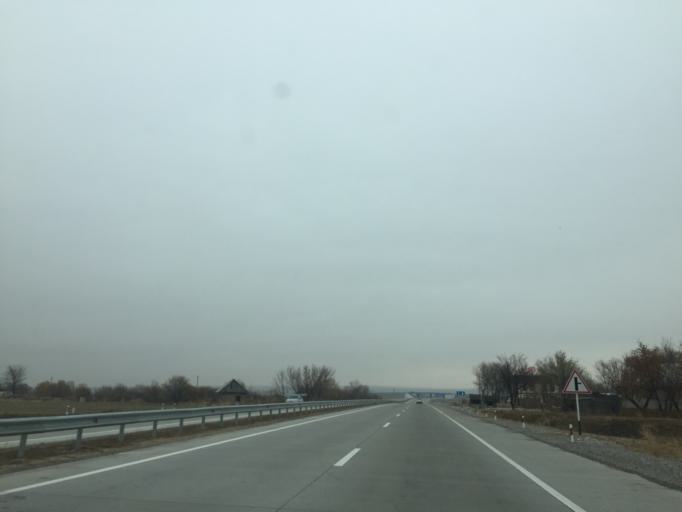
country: KZ
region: Ongtustik Qazaqstan
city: Aksu
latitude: 42.4711
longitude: 69.8050
